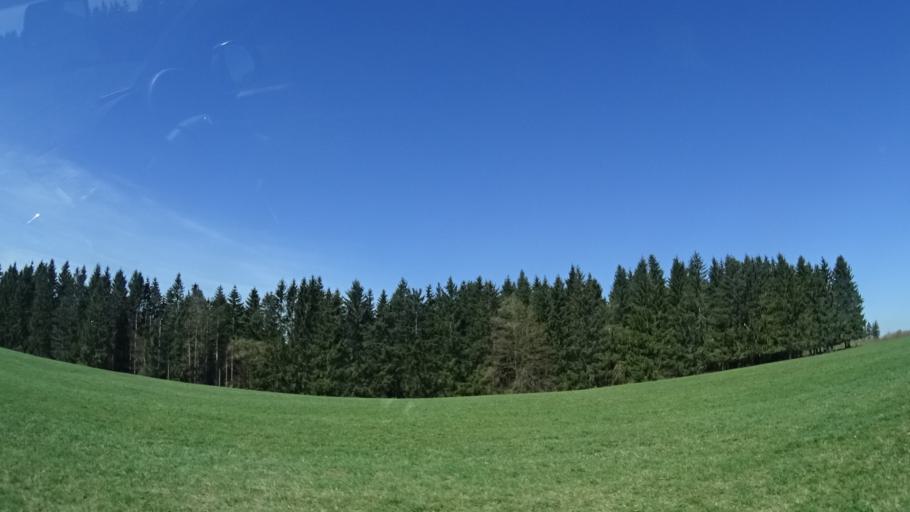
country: DE
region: Thuringia
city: Frauenwald
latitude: 50.5676
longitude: 10.8608
